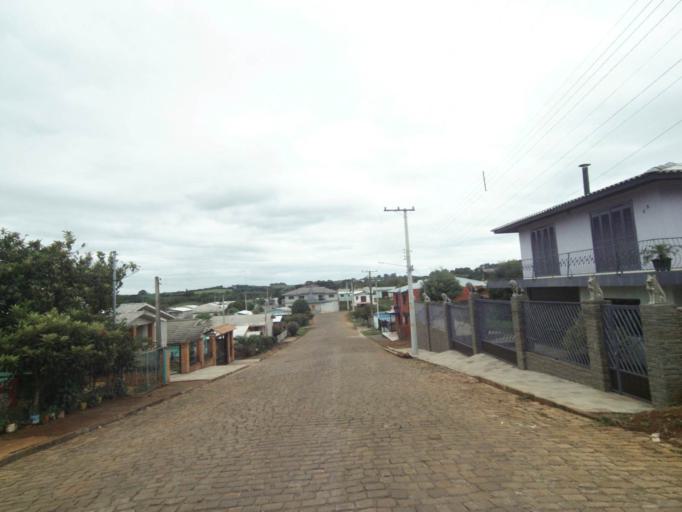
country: BR
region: Rio Grande do Sul
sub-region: Lagoa Vermelha
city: Lagoa Vermelha
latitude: -28.2121
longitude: -51.5063
